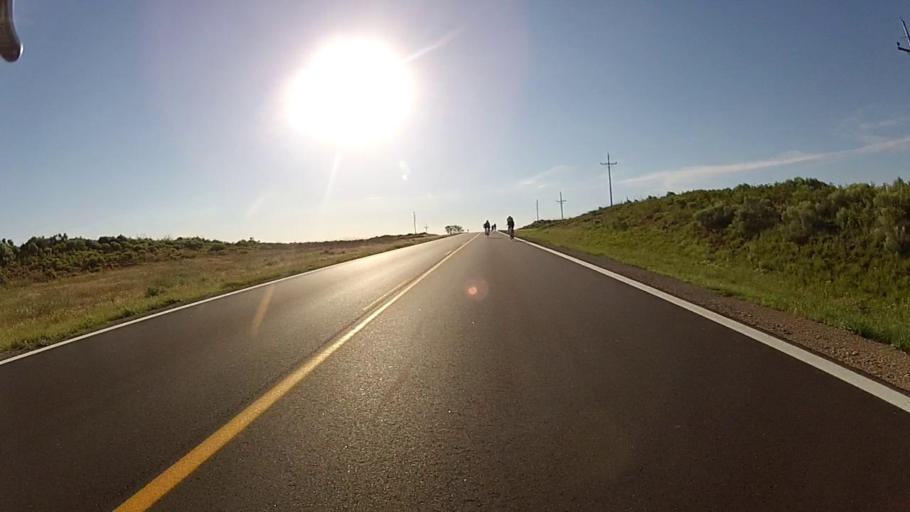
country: US
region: Kansas
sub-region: Comanche County
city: Coldwater
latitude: 37.2815
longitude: -99.0577
